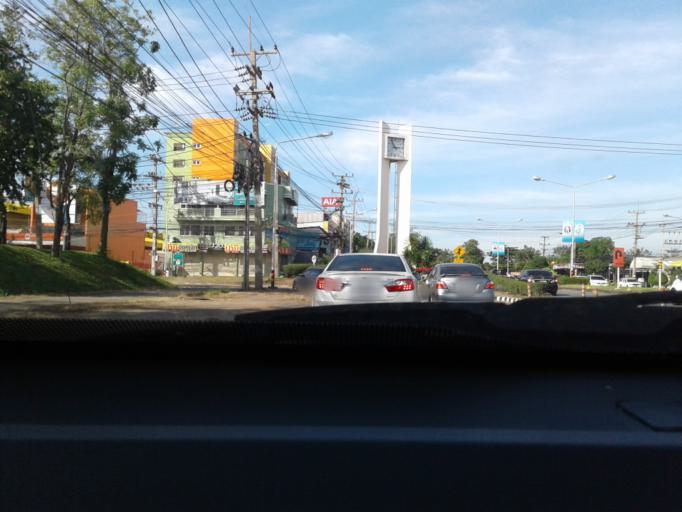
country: TH
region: Nakhon Pathom
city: Salaya
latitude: 13.8006
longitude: 100.3270
